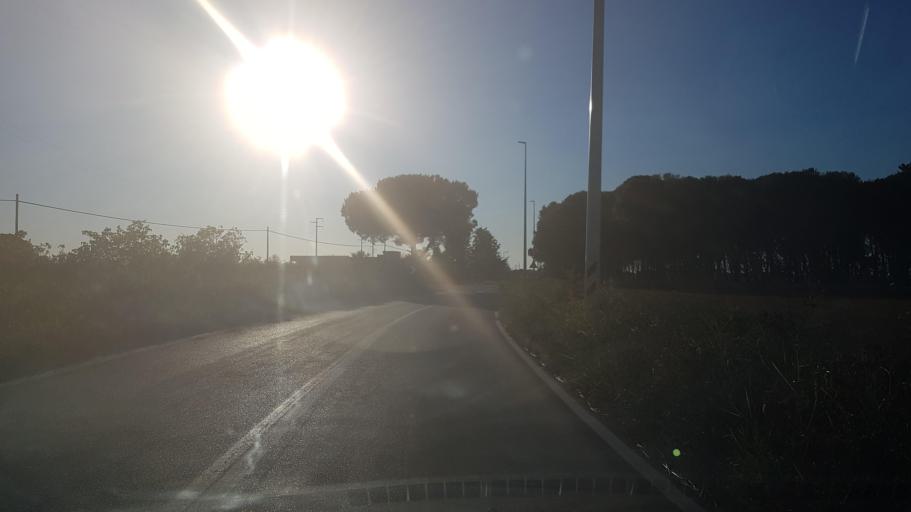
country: IT
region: Apulia
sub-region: Provincia di Lecce
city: Struda
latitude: 40.3270
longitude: 18.3123
